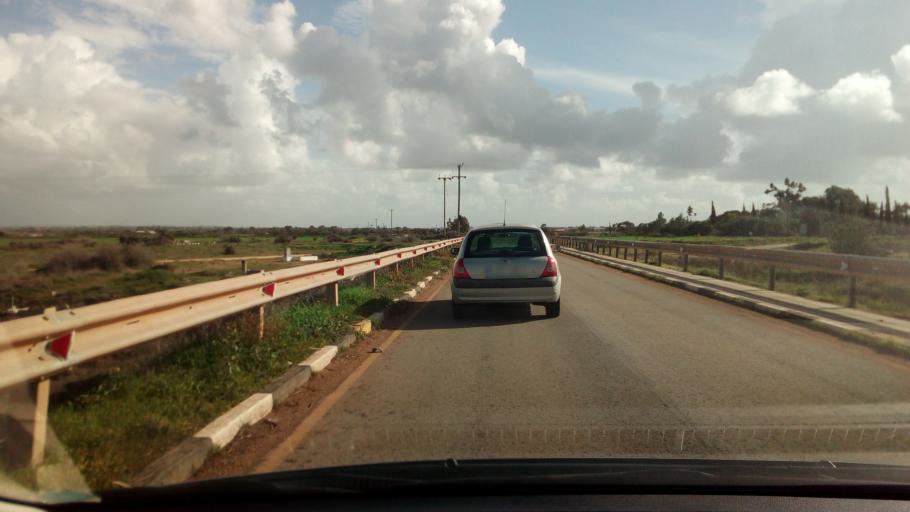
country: CY
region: Ammochostos
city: Achna
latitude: 35.0551
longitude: 33.8146
